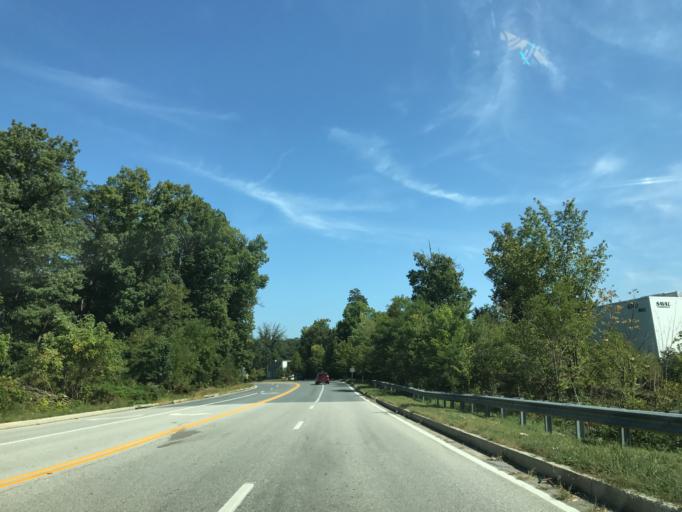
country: US
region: Maryland
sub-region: Anne Arundel County
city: Jessup
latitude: 39.1826
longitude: -76.7616
